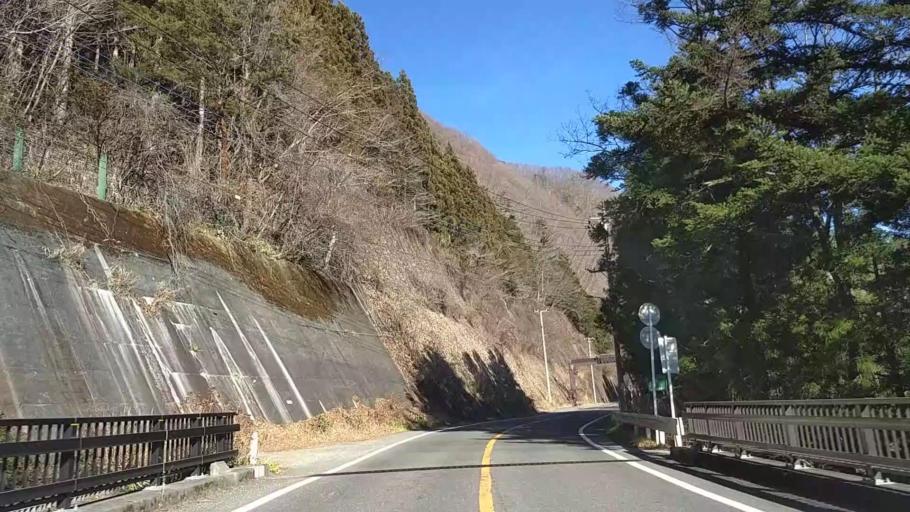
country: JP
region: Yamanashi
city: Uenohara
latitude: 35.5360
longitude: 139.0568
